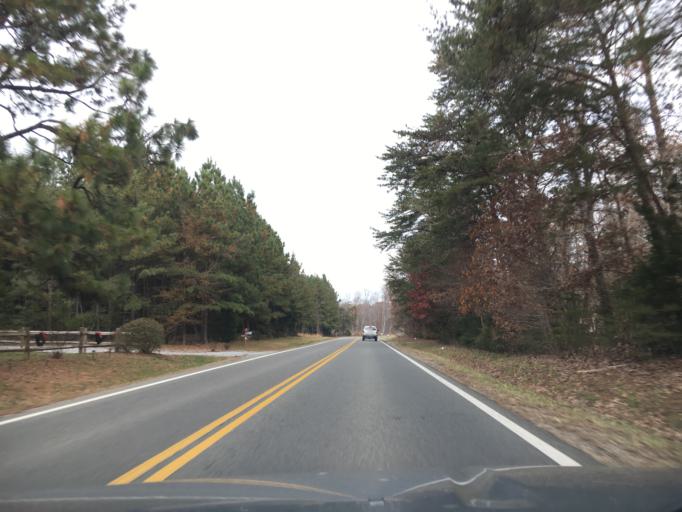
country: US
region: Virginia
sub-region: Prince Edward County
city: Farmville
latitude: 37.4207
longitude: -78.3523
